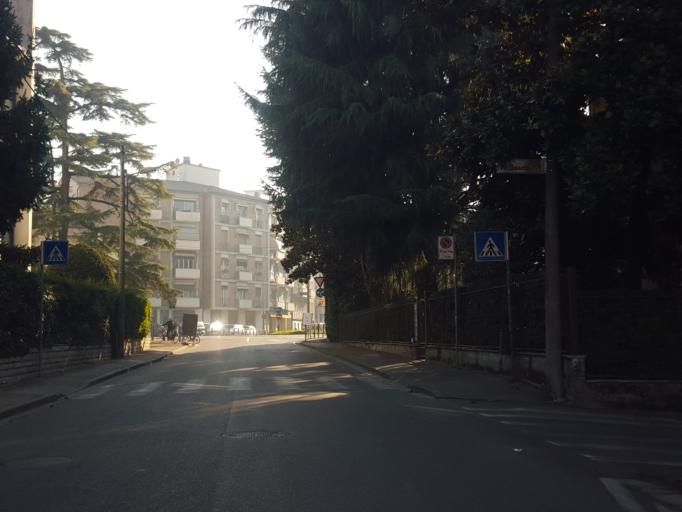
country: IT
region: Veneto
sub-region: Provincia di Vicenza
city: Vicenza
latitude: 45.5477
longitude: 11.5532
